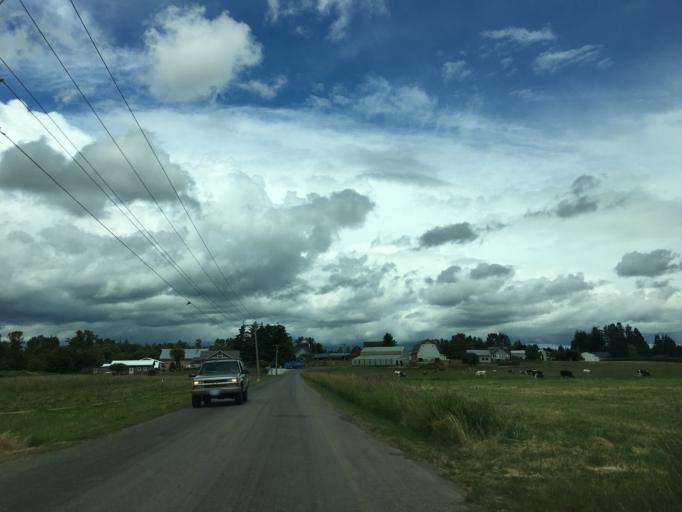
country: US
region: Washington
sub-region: Whatcom County
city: Lynden
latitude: 48.9278
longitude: -122.4963
